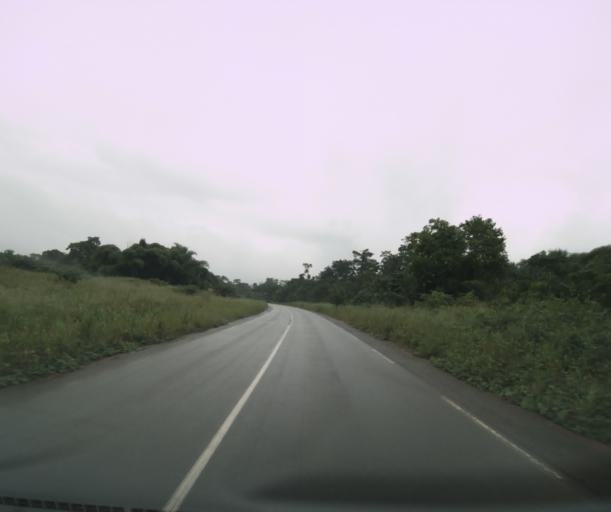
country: CM
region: Littoral
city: Dizangue
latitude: 3.4621
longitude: 10.1296
